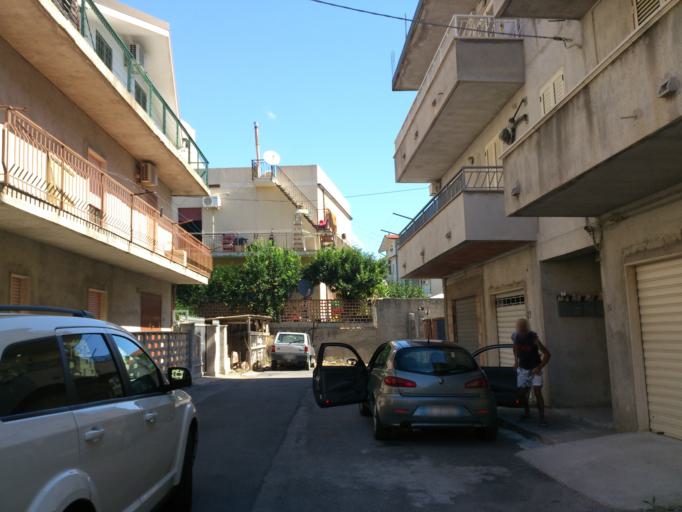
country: IT
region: Calabria
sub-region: Provincia di Reggio Calabria
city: Monasterace Marina
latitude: 38.4350
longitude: 16.5727
